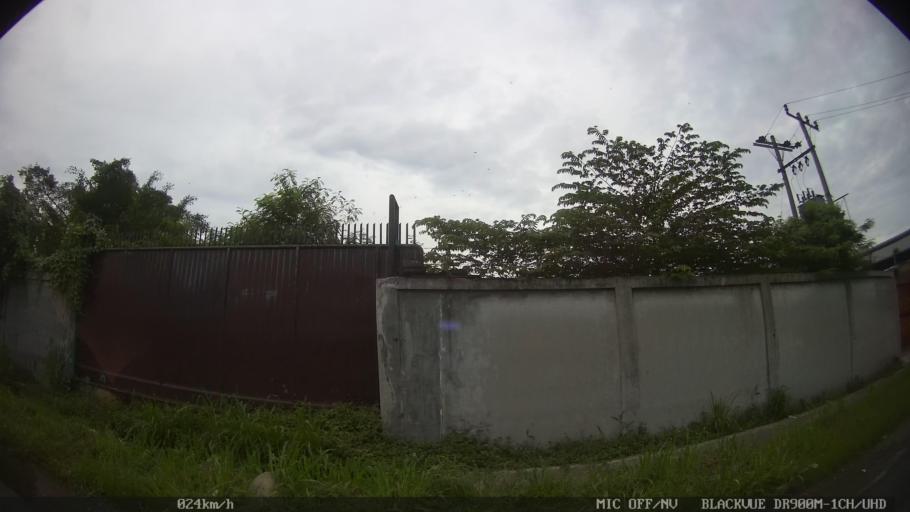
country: ID
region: North Sumatra
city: Sunggal
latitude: 3.6143
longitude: 98.5864
